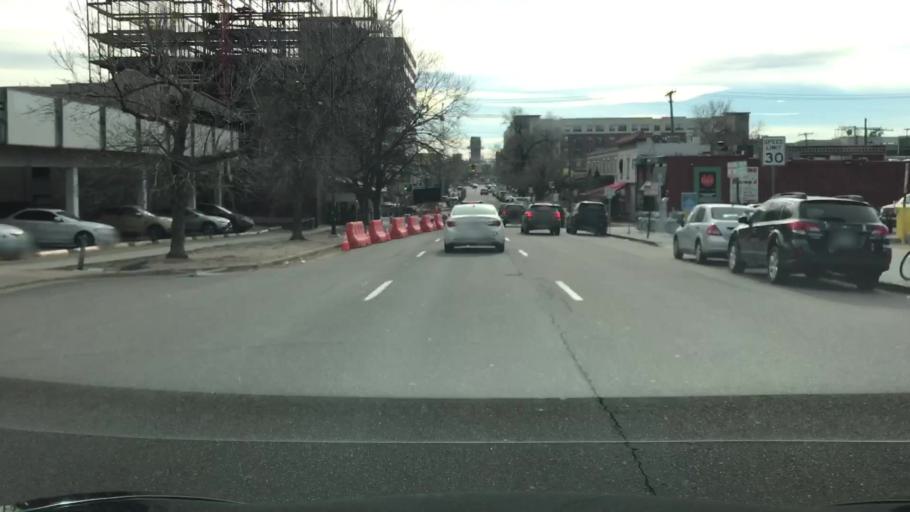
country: US
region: Colorado
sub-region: Denver County
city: Denver
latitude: 39.7281
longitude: -104.9836
